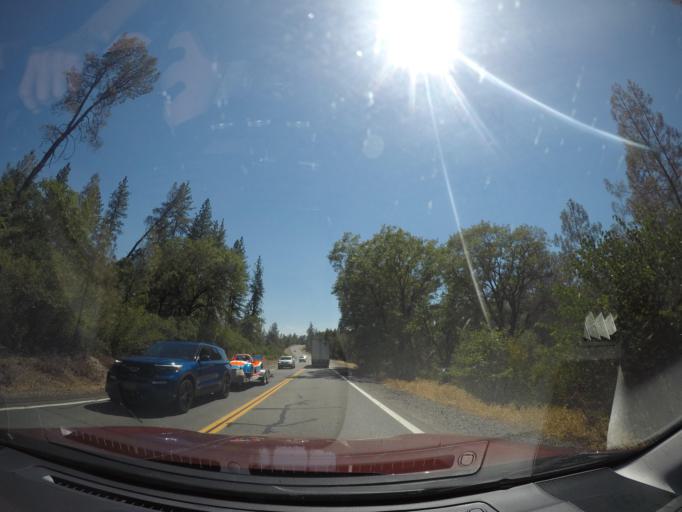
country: US
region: California
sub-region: Shasta County
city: Bella Vista
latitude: 40.7027
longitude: -122.0969
